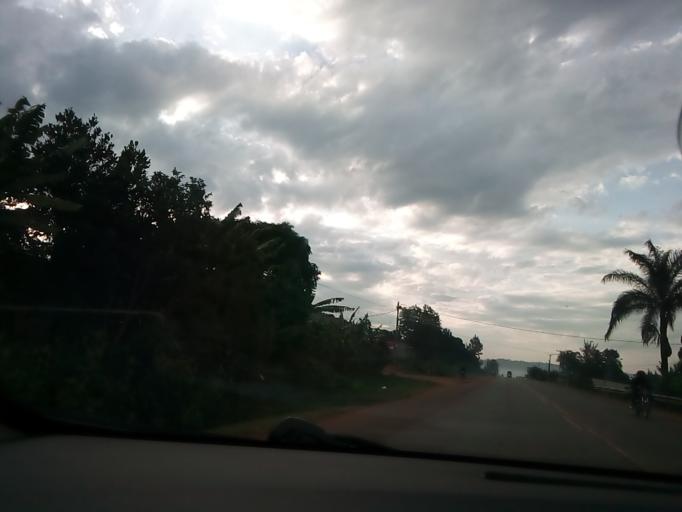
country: UG
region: Central Region
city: Masaka
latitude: -0.3370
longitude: 31.6976
